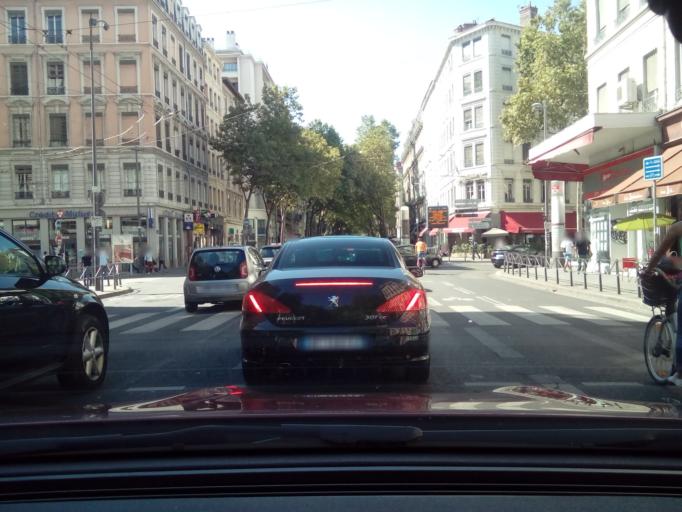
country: FR
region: Rhone-Alpes
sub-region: Departement du Rhone
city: Lyon
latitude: 45.7538
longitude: 4.8475
